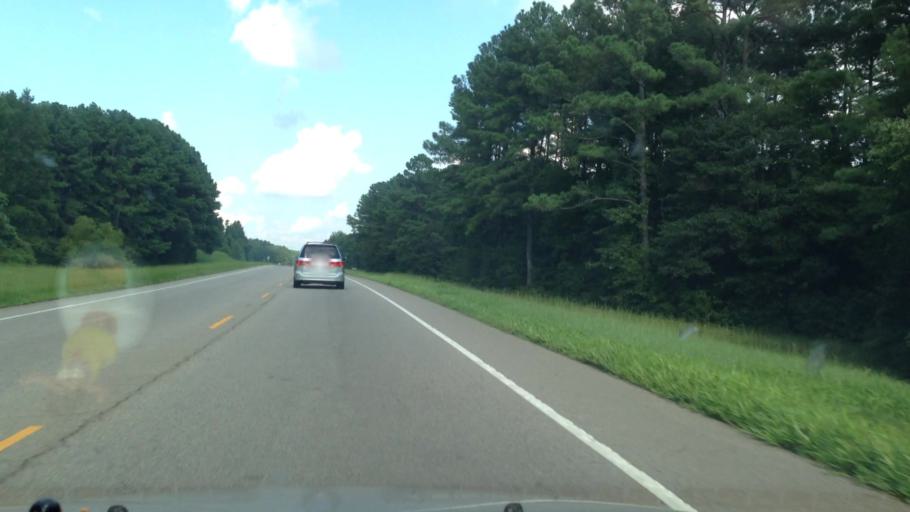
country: US
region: North Carolina
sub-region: Lee County
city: Broadway
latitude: 35.4378
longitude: -79.0593
